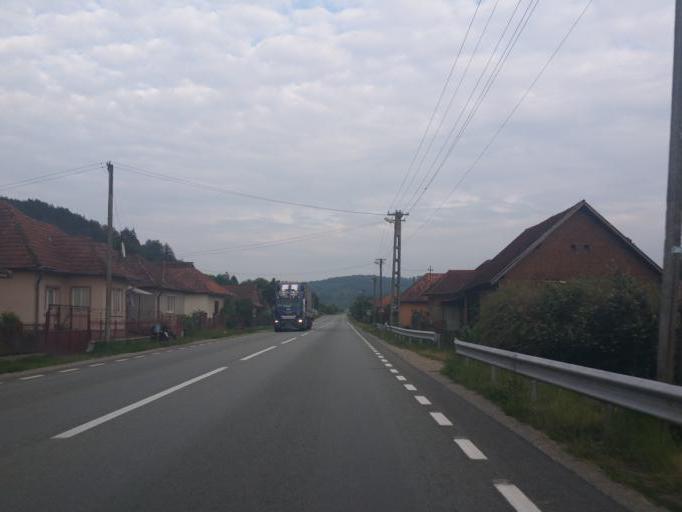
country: RO
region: Salaj
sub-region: Comuna Sanmihaiu Almasului
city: Sanmihaiu Almasului
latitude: 46.9547
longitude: 23.3489
